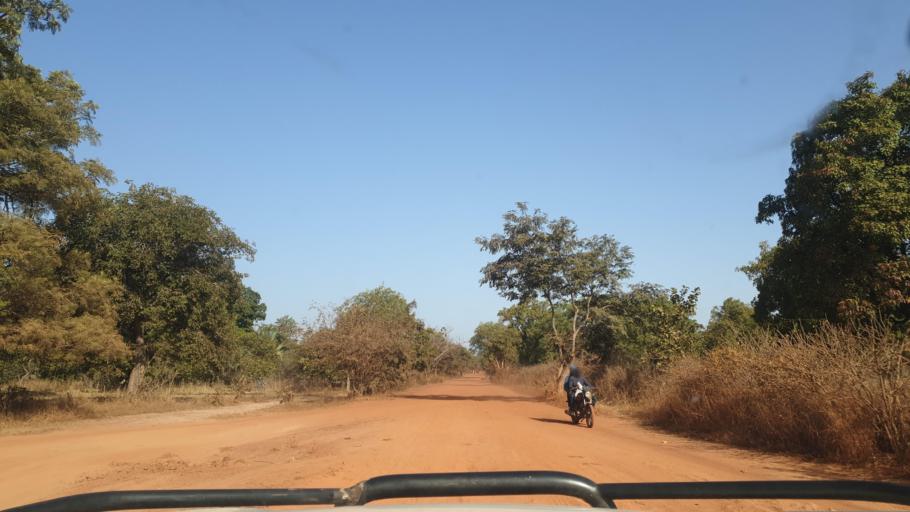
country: ML
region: Sikasso
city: Kolondieba
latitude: 11.7392
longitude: -6.8947
